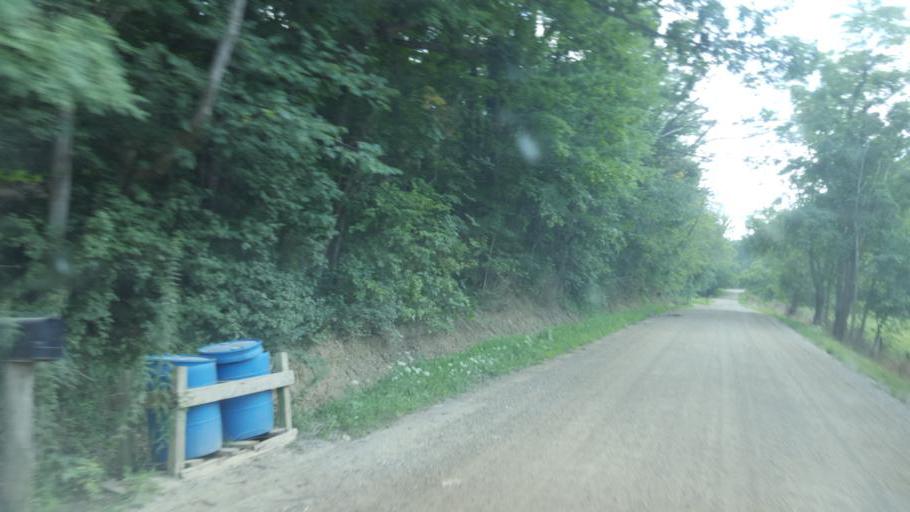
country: US
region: Ohio
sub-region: Knox County
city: Mount Vernon
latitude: 40.3417
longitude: -82.5716
